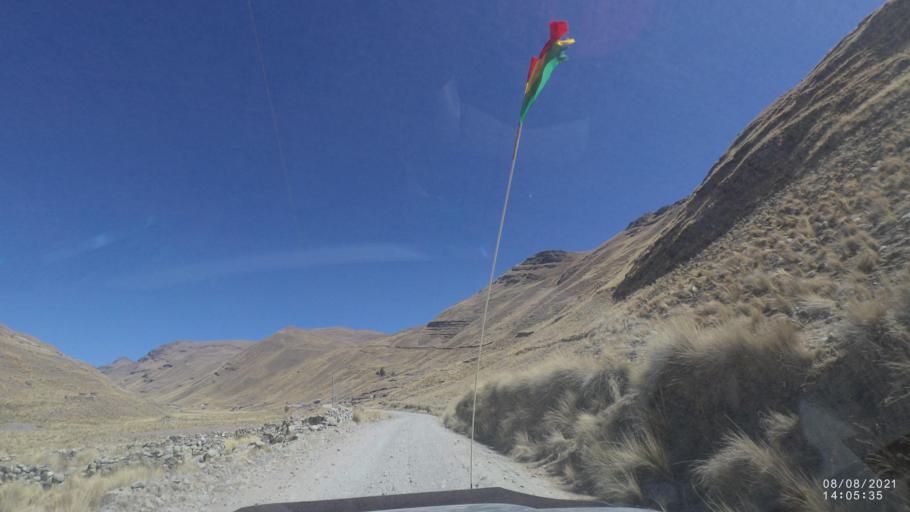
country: BO
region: Cochabamba
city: Sipe Sipe
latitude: -17.1182
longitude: -66.4397
